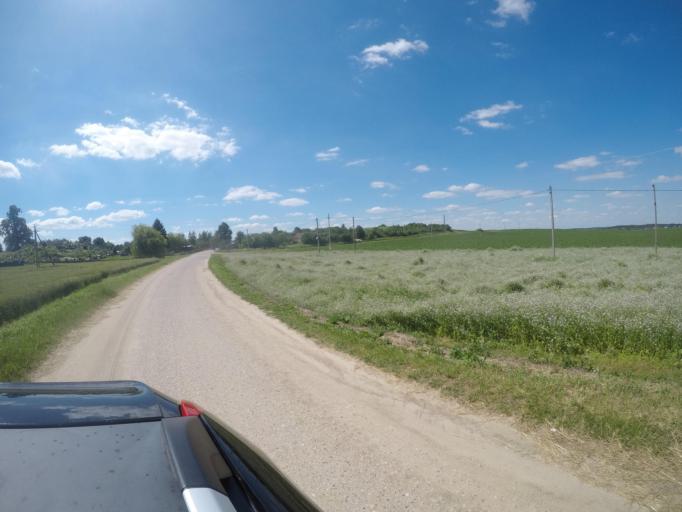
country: BY
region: Grodnenskaya
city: Hrodna
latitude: 53.7300
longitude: 23.8513
